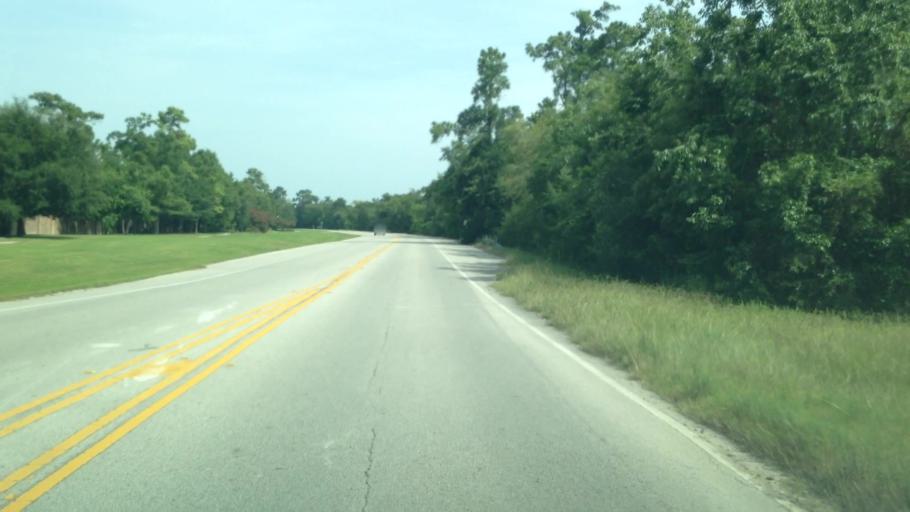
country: US
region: Texas
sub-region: Harris County
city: Atascocita
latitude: 29.9294
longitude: -95.1746
